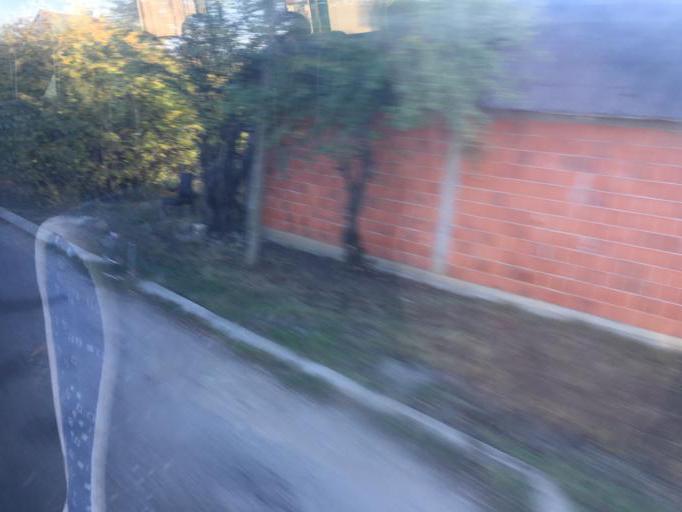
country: XK
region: Pristina
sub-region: Komuna e Drenasit
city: Glogovac
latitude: 42.5971
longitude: 20.8929
